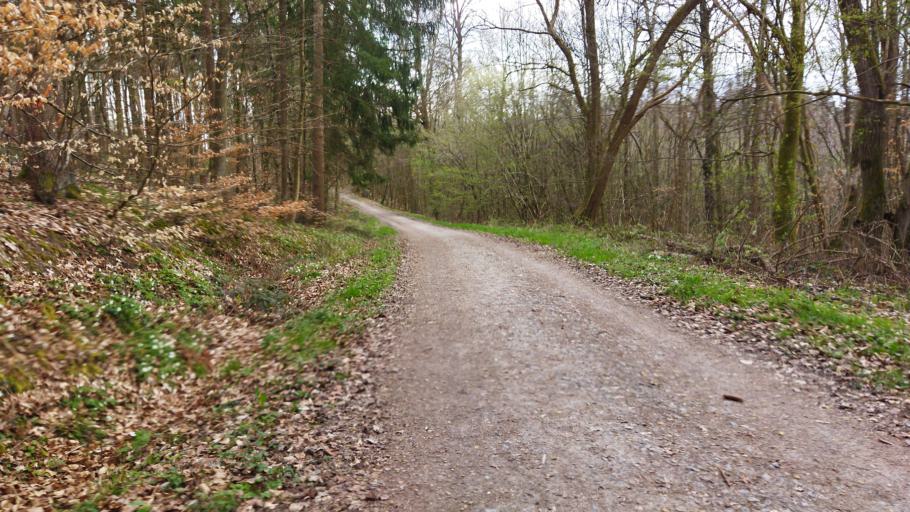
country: DE
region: Baden-Wuerttemberg
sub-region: Regierungsbezirk Stuttgart
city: Erlenbach
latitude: 49.2041
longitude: 9.2871
